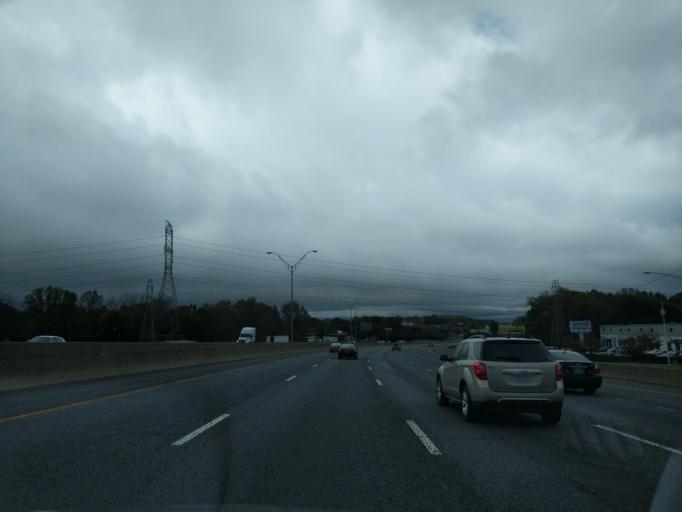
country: US
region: North Carolina
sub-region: Mecklenburg County
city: Charlotte
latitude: 35.2663
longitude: -80.8737
